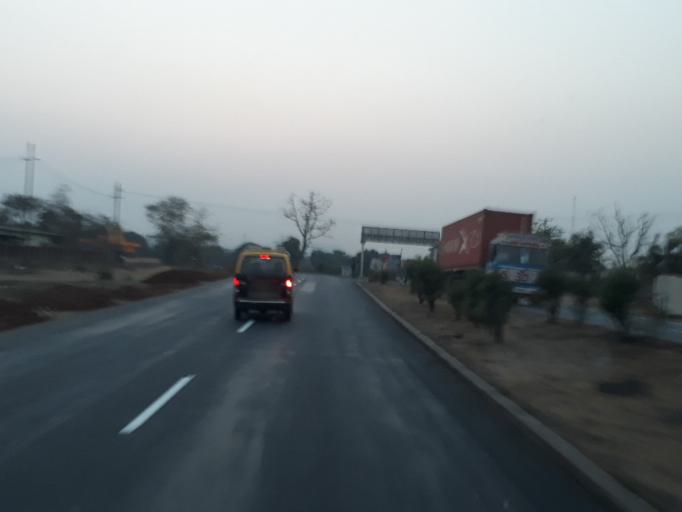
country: IN
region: Maharashtra
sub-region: Raigarh
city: Matheran
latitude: 18.9013
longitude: 73.2317
